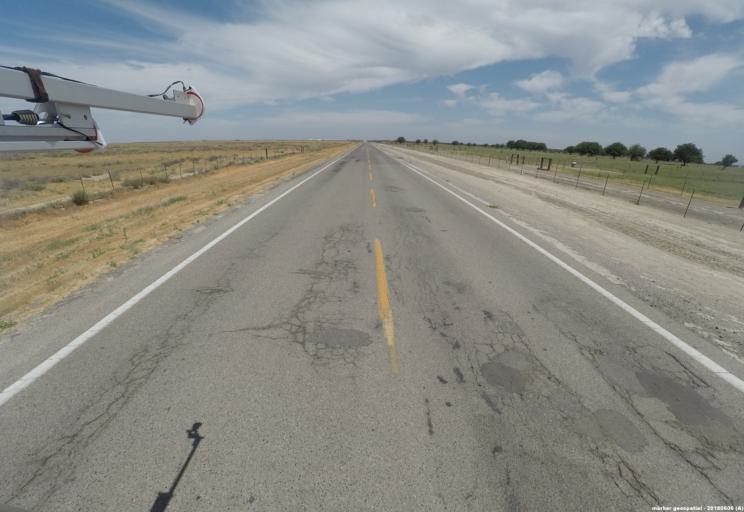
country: US
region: California
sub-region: Fresno County
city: Firebaugh
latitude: 36.9316
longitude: -120.3823
